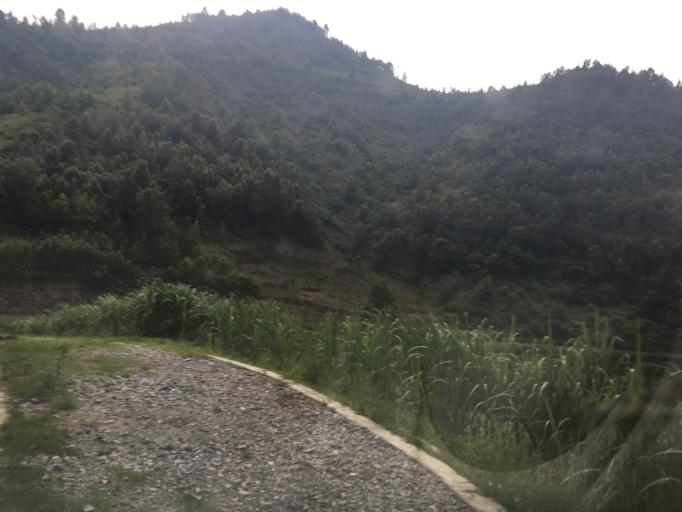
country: CN
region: Guangxi Zhuangzu Zizhiqu
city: Xinzhou
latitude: 25.1698
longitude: 105.6980
